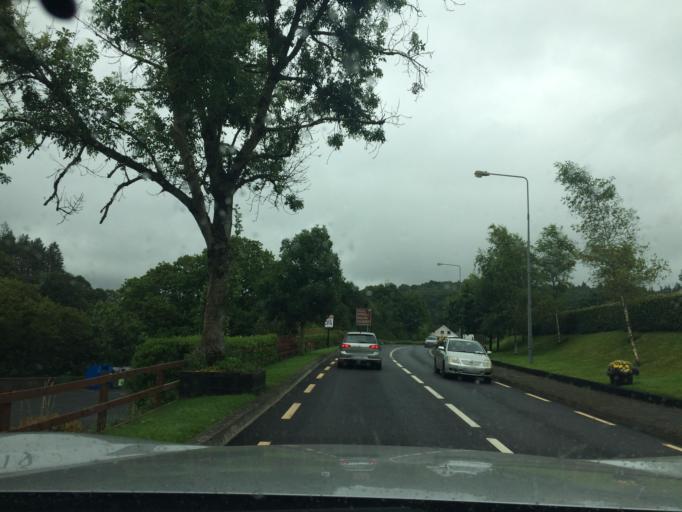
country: IE
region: Munster
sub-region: South Tipperary
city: Cluain Meala
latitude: 52.2669
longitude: -7.7145
